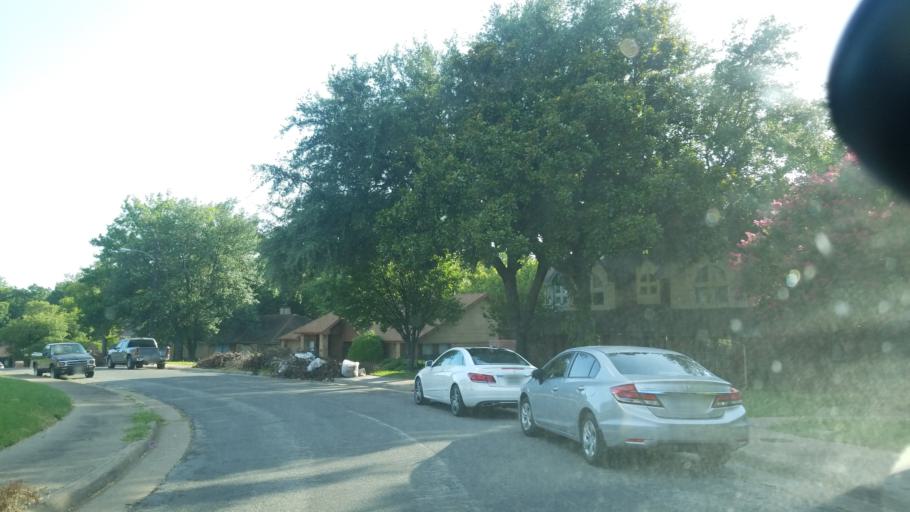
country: US
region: Texas
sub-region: Dallas County
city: Highland Park
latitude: 32.7822
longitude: -96.7091
